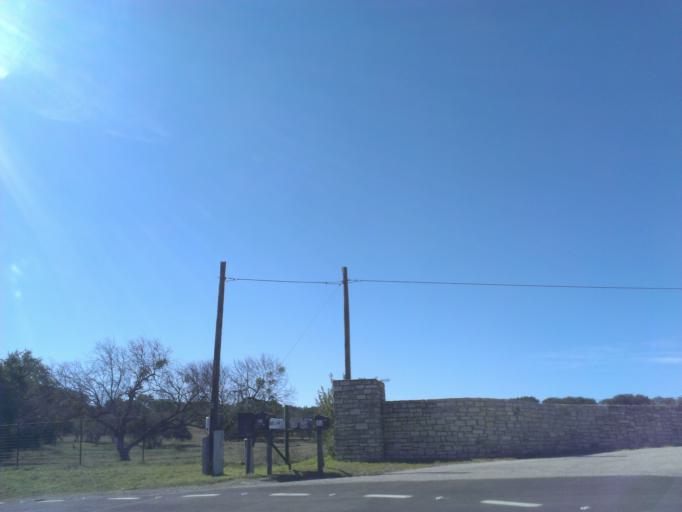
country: US
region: Texas
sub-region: Travis County
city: Briarcliff
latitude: 30.4668
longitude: -98.1217
